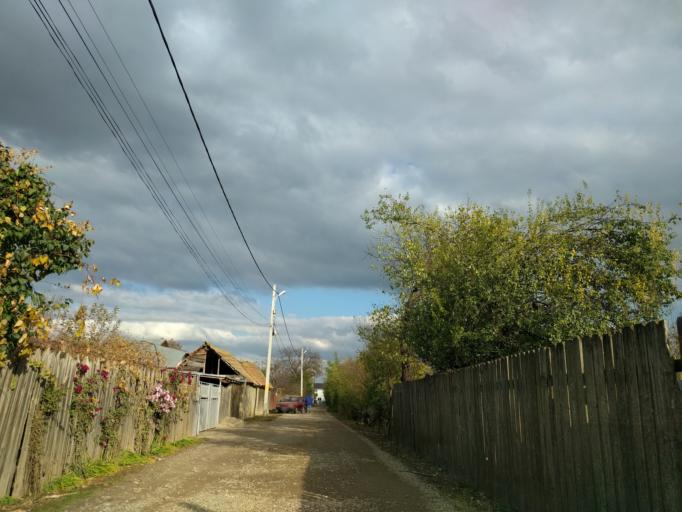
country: RO
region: Ilfov
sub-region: Comuna Branesti
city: Branesti
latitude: 44.4522
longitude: 26.3449
